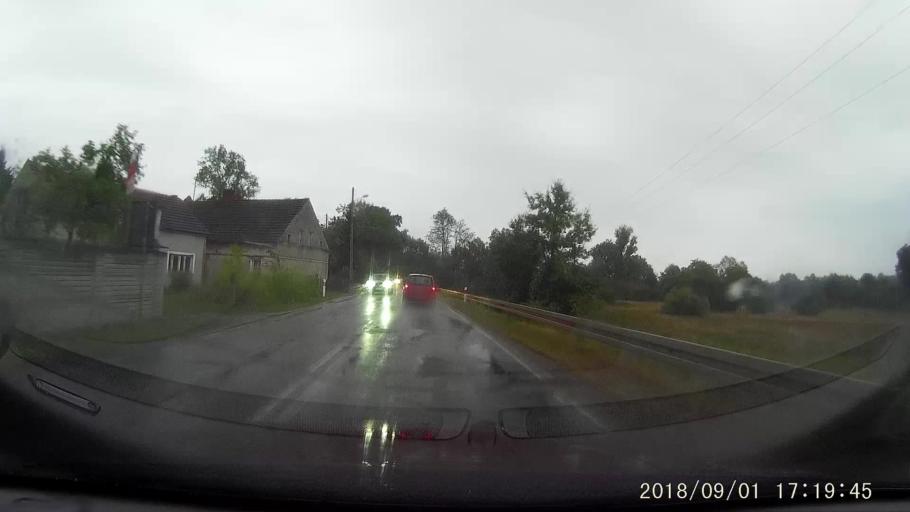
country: PL
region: Lubusz
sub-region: Powiat zielonogorski
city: Nowogrod Bobrzanski
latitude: 51.7296
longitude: 15.2741
